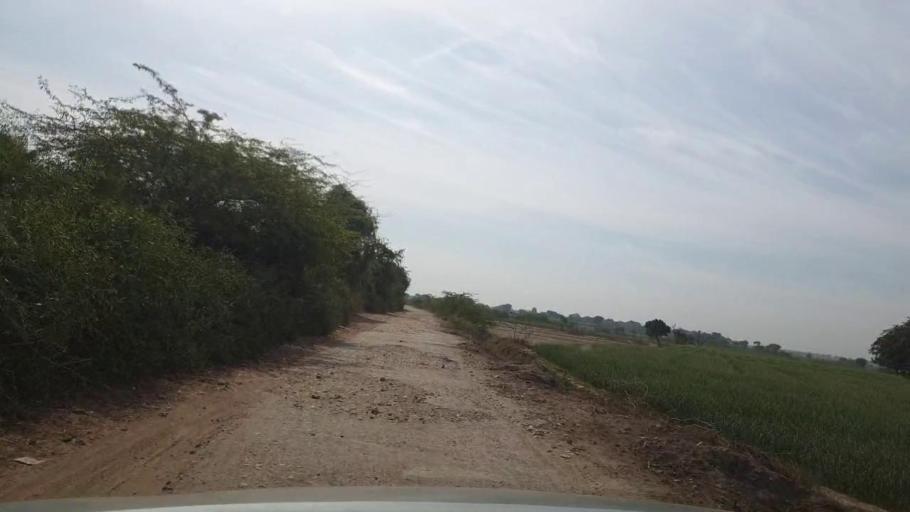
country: PK
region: Sindh
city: Kunri
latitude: 25.1598
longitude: 69.5973
